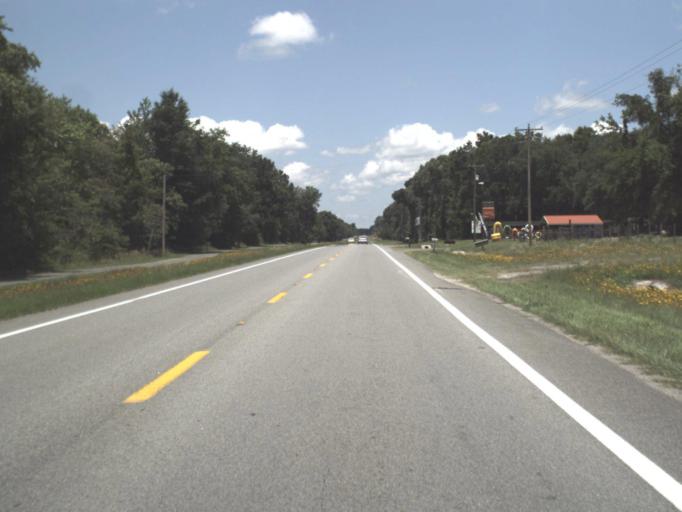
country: US
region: Florida
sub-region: Alachua County
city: High Springs
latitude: 29.9332
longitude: -82.7296
